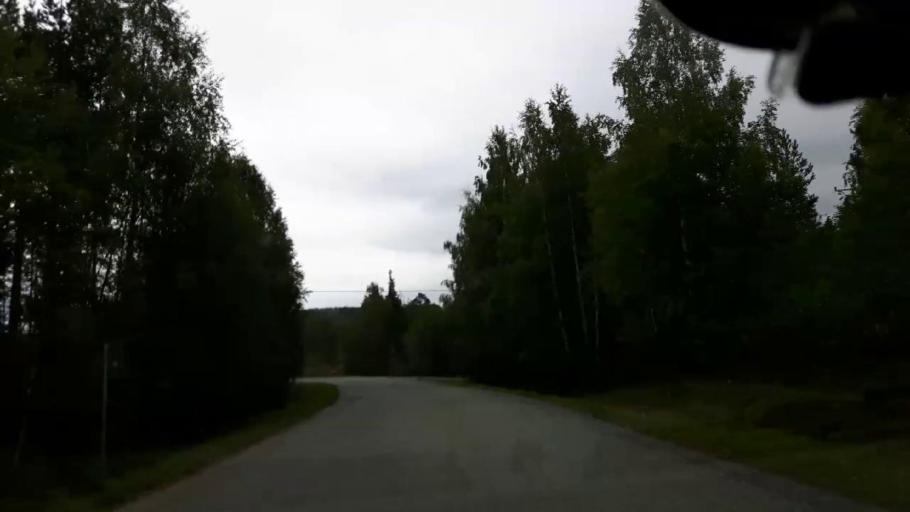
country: SE
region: Vaesternorrland
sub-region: Ange Kommun
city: Fransta
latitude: 62.7761
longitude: 16.2259
